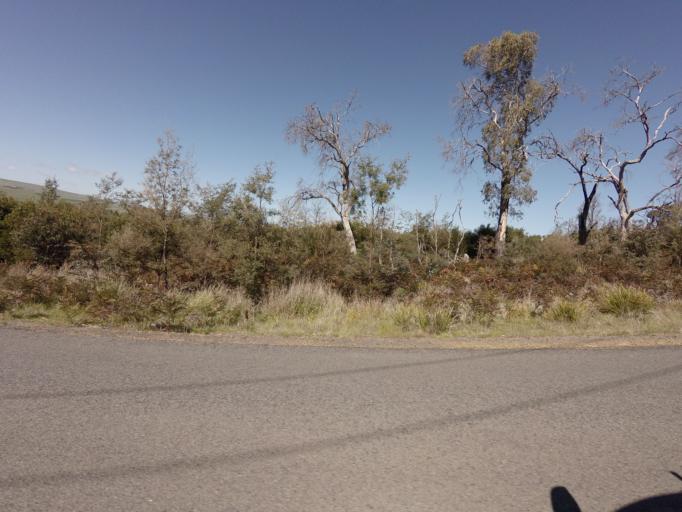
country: AU
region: Tasmania
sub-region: Derwent Valley
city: New Norfolk
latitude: -42.5393
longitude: 146.7211
